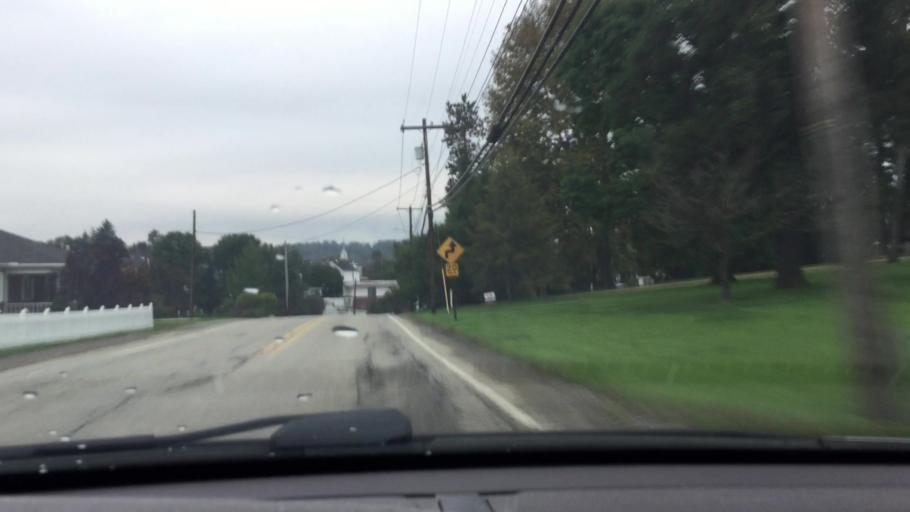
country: US
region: Pennsylvania
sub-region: Westmoreland County
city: Lynnwood-Pricedale
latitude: 40.1282
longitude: -79.8522
